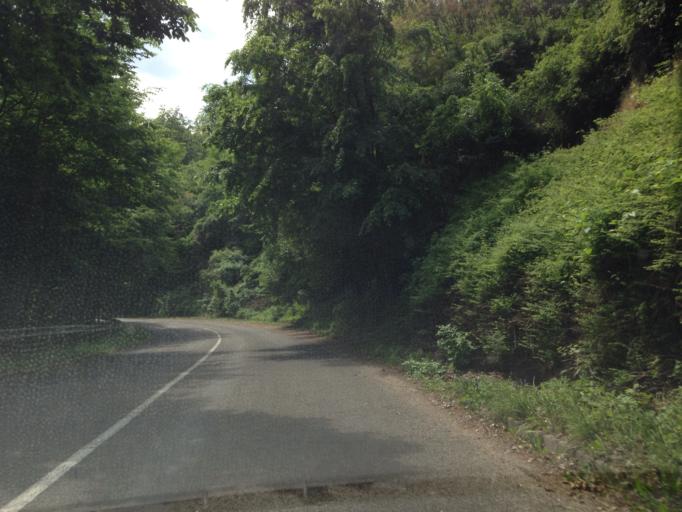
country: HU
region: Pest
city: Visegrad
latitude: 47.7316
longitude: 18.9557
